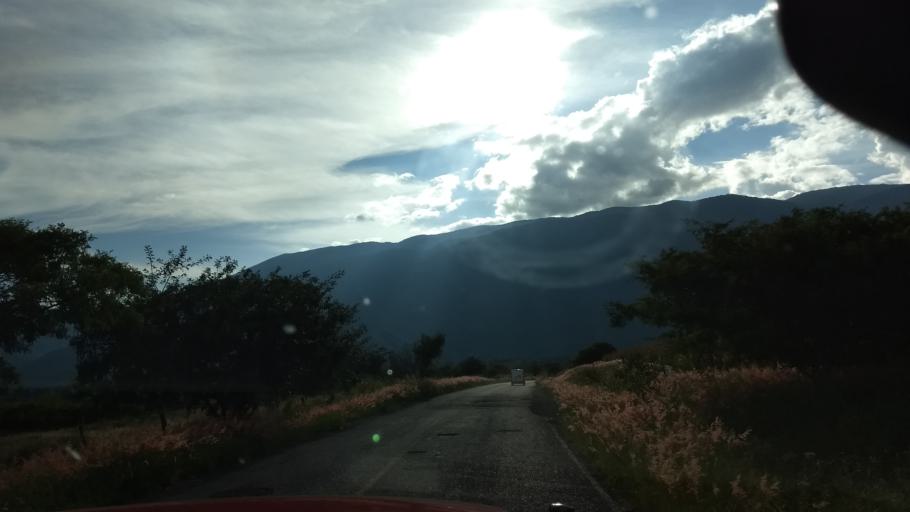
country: MX
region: Colima
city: Suchitlan
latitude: 19.4530
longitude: -103.8080
